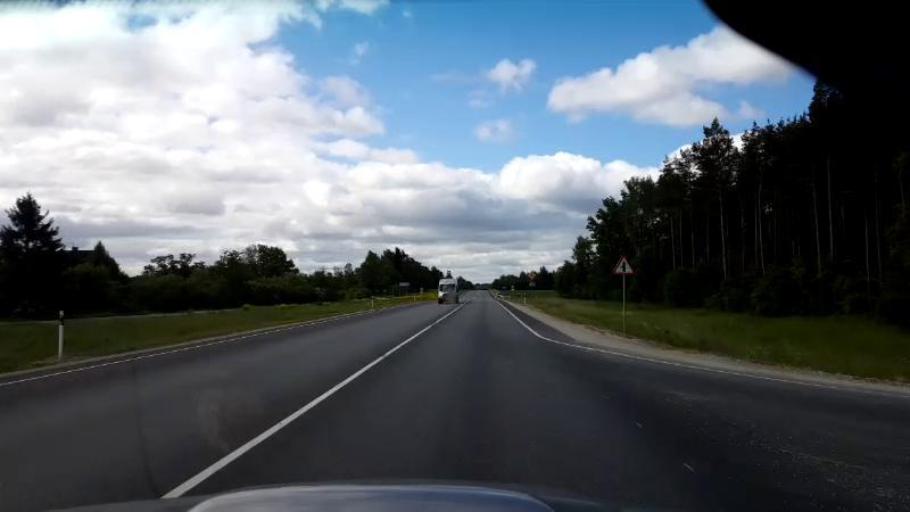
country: EE
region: Harju
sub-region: Nissi vald
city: Riisipere
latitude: 59.0593
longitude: 24.4479
